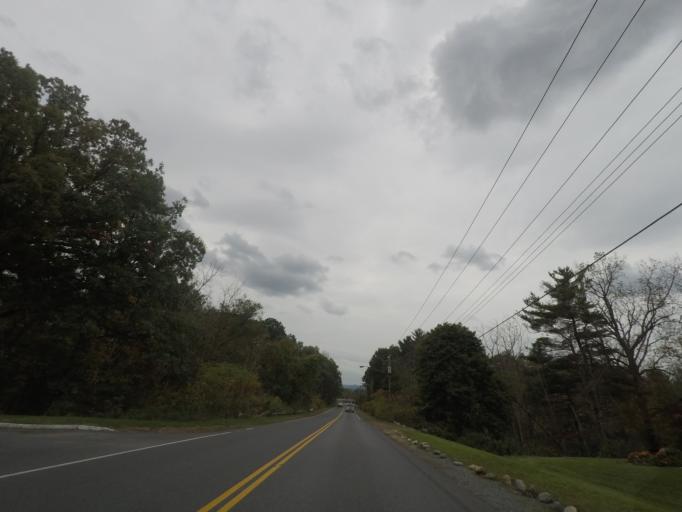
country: US
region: New York
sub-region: Albany County
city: McKownville
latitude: 42.6622
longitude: -73.8223
